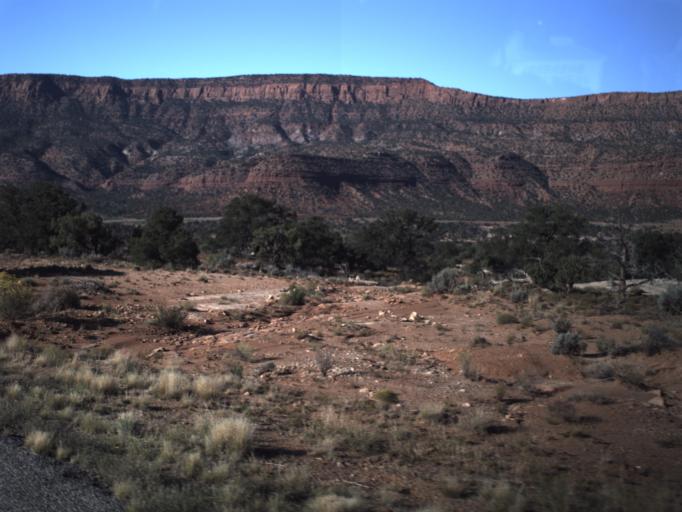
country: US
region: Utah
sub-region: San Juan County
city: Blanding
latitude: 37.6450
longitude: -110.1446
